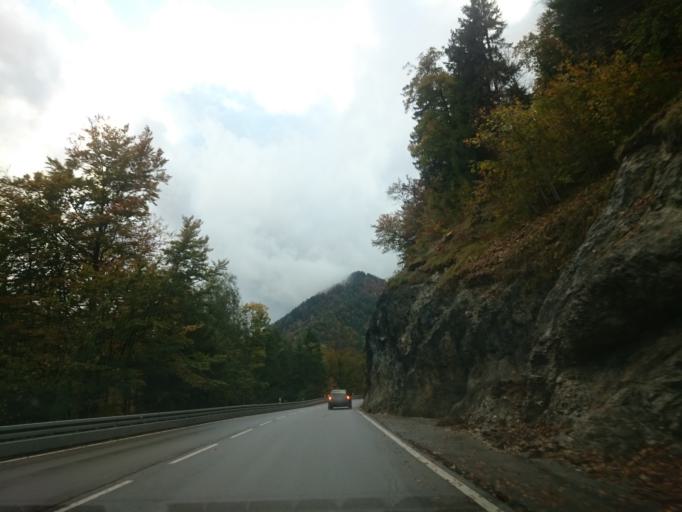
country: DE
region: Bavaria
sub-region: Upper Bavaria
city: Ettal
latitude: 47.5605
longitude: 11.1183
